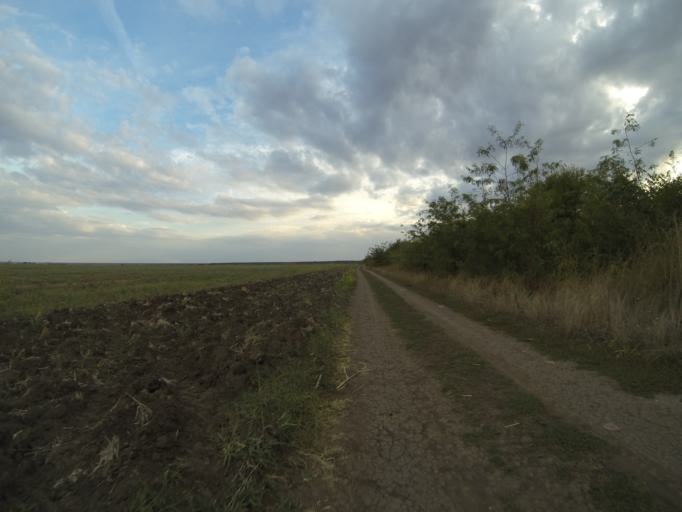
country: RO
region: Dolj
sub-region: Comuna Ceratu
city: Ceratu
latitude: 44.1043
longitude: 23.6928
